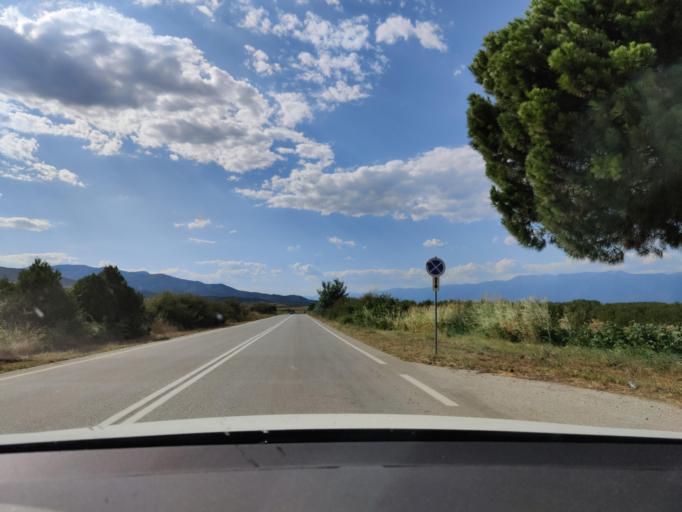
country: GR
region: Central Macedonia
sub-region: Nomos Serron
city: Strymoniko
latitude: 41.0930
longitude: 23.2756
